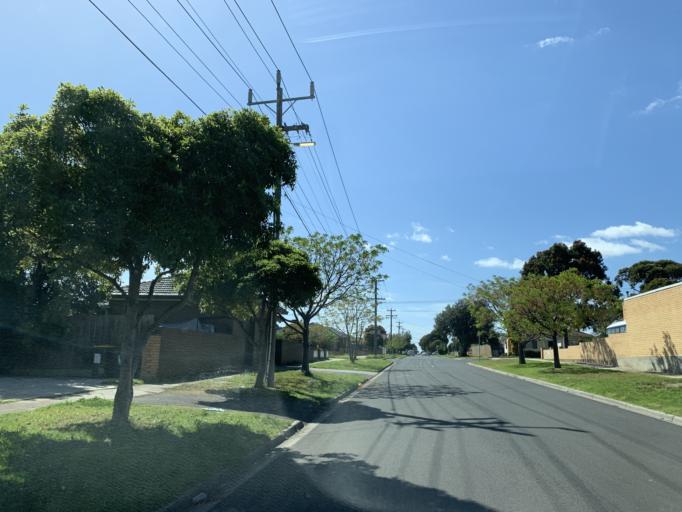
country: AU
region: Victoria
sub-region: Brimbank
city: Saint Albans
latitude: -37.7343
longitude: 144.7987
